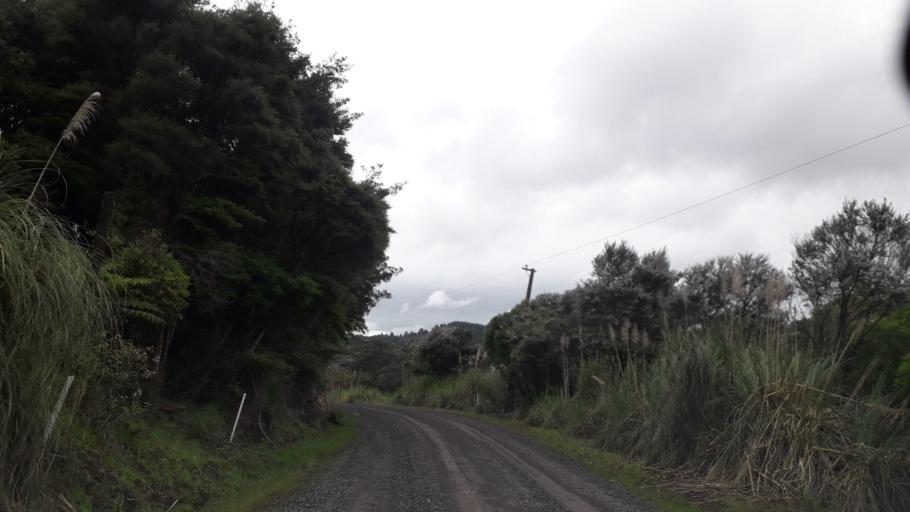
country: NZ
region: Northland
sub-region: Far North District
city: Kaitaia
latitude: -35.3863
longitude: 173.4062
